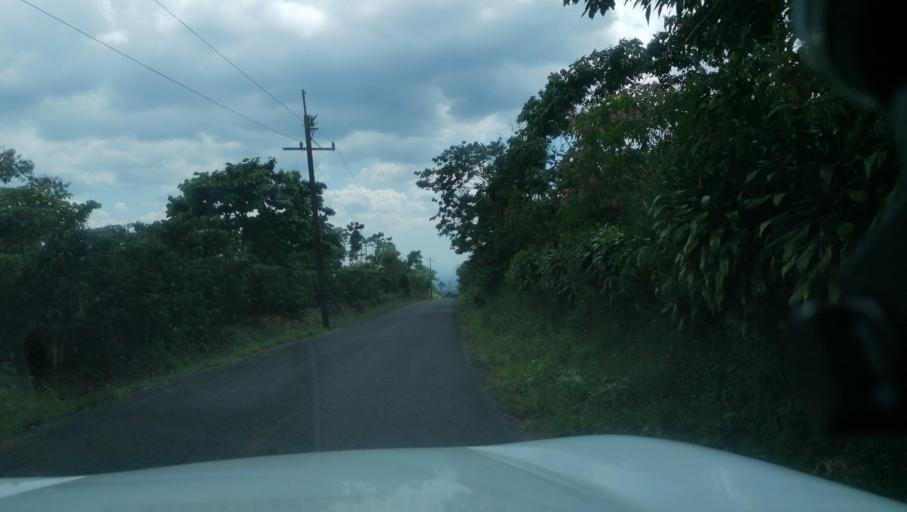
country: MX
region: Chiapas
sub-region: Cacahoatan
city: Benito Juarez
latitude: 15.0555
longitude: -92.1515
